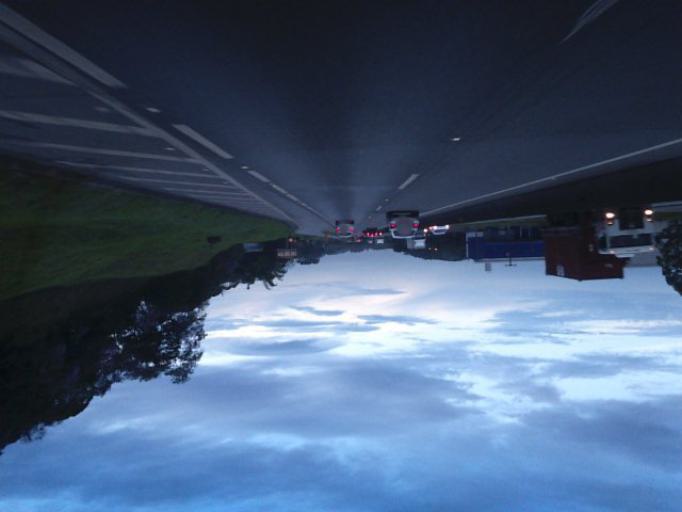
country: BR
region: Santa Catarina
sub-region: Joinville
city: Joinville
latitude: -26.1614
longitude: -48.9075
